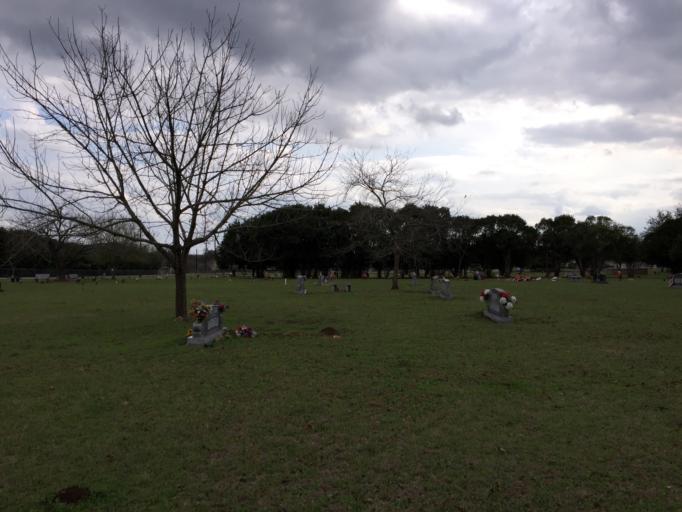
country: US
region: Texas
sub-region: Travis County
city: Manchaca
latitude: 30.1439
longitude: -97.8220
